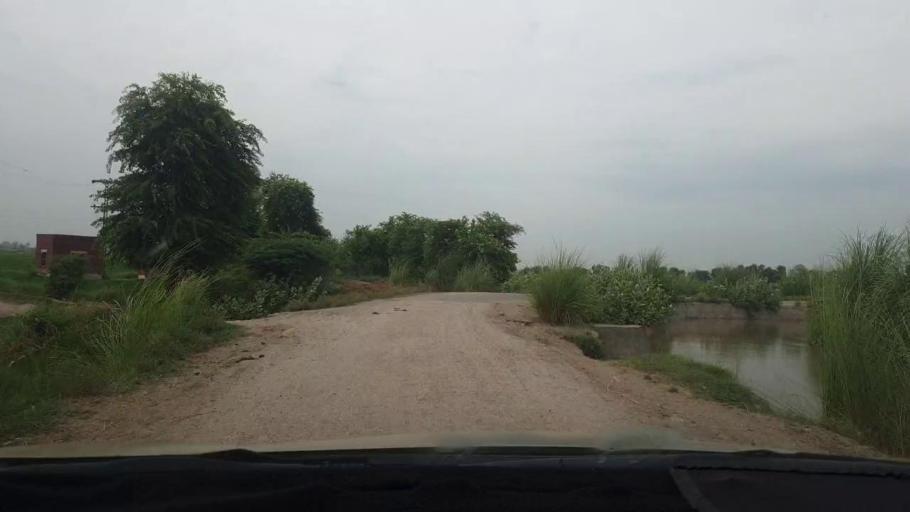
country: PK
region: Sindh
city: Naudero
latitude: 27.6785
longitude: 68.3422
